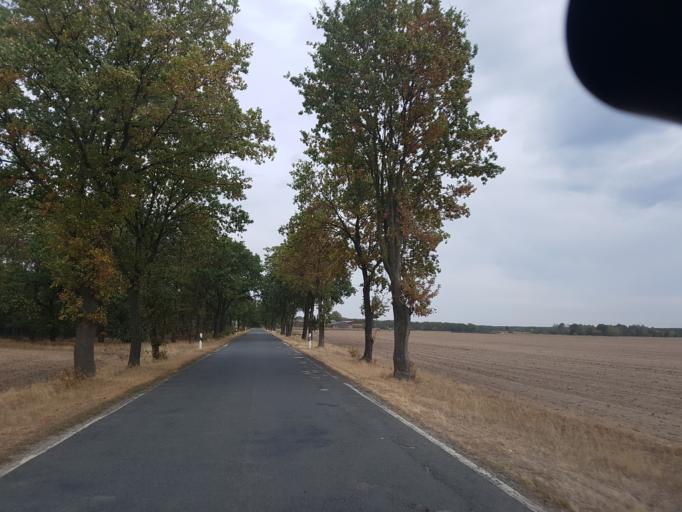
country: DE
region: Saxony-Anhalt
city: Annaburg
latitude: 51.7701
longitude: 13.0689
